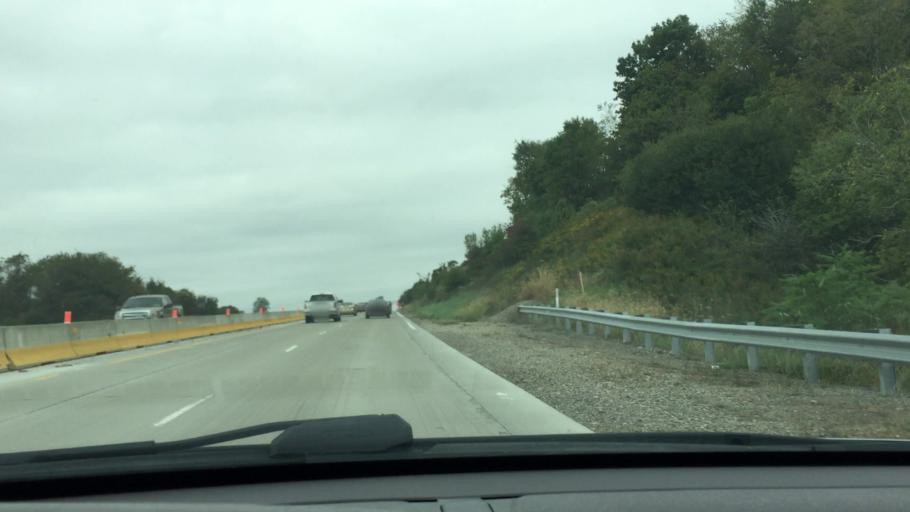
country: US
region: Pennsylvania
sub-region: Allegheny County
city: Enlow
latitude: 40.4704
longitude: -80.2461
